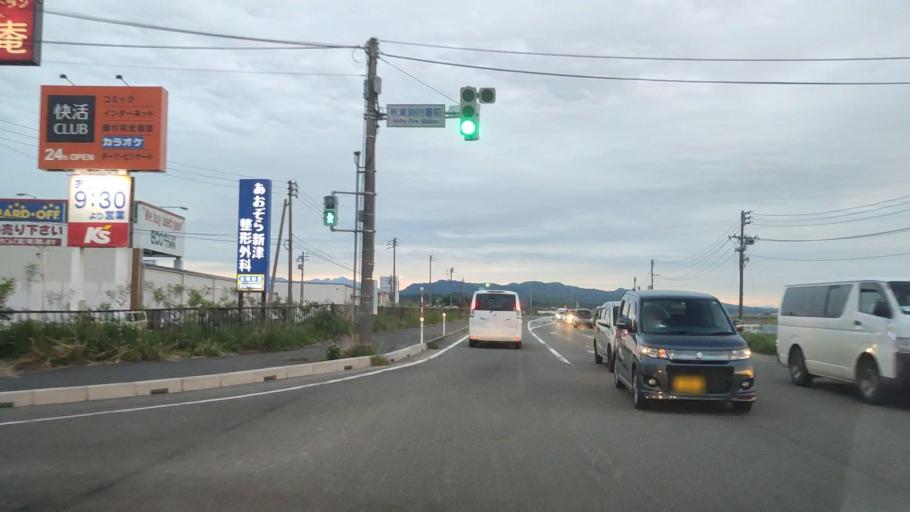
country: JP
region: Niigata
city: Niitsu-honcho
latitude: 37.7863
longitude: 139.1120
